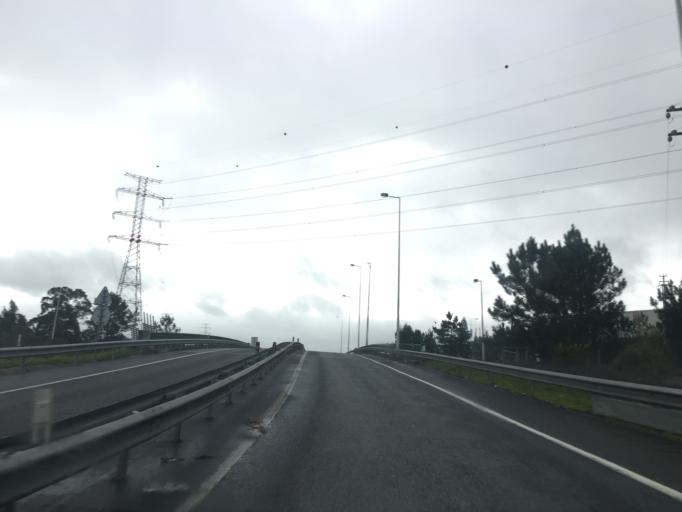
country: PT
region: Leiria
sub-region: Leiria
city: Leiria
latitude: 39.7410
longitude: -8.7695
